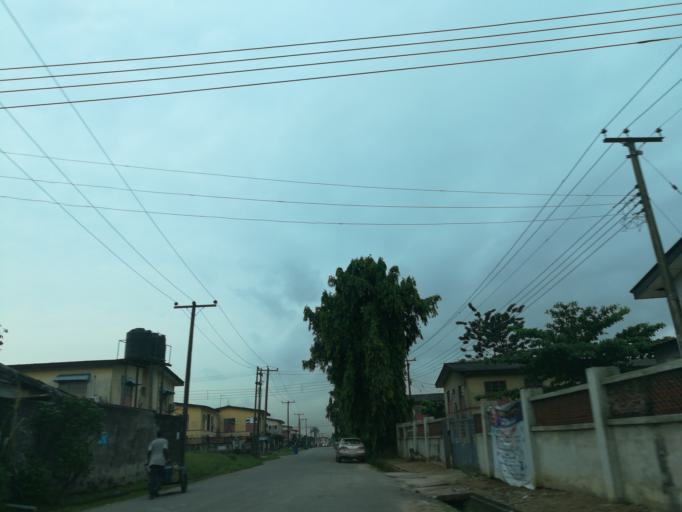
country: NG
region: Rivers
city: Port Harcourt
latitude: 4.8197
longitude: 7.0258
